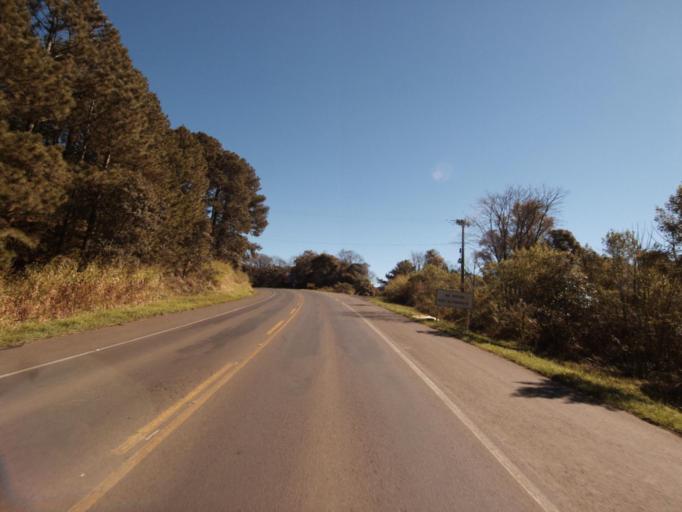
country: BR
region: Santa Catarina
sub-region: Joacaba
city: Joacaba
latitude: -27.1591
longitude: -51.5859
